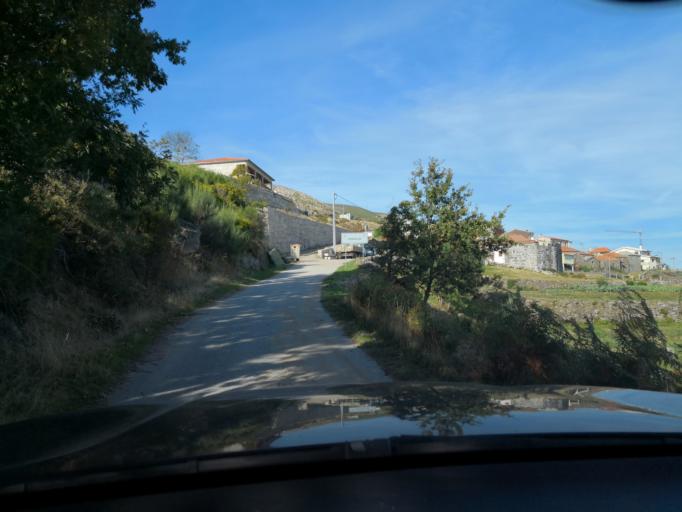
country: PT
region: Vila Real
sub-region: Vila Real
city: Vila Real
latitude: 41.3469
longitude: -7.7644
